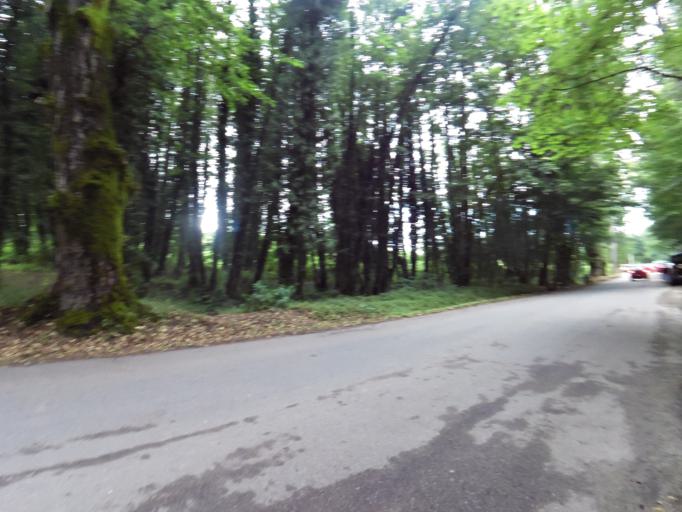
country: IT
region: Calabria
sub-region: Provincia di Vibo-Valentia
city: Serra San Bruno
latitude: 38.5658
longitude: 16.3166
